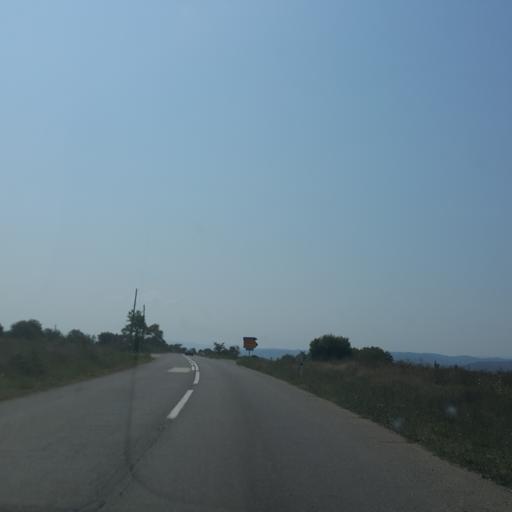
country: RS
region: Central Serbia
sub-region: Zajecarski Okrug
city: Knjazevac
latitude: 43.7080
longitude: 22.3043
